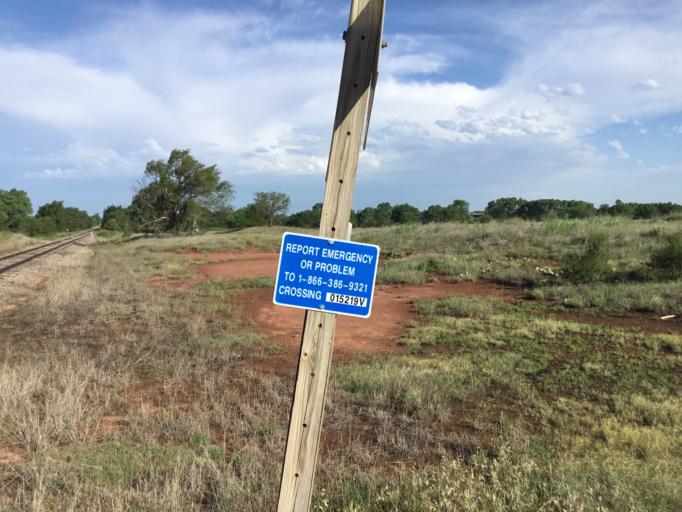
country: US
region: Kansas
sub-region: Sedgwick County
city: Cheney
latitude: 37.6118
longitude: -97.9479
